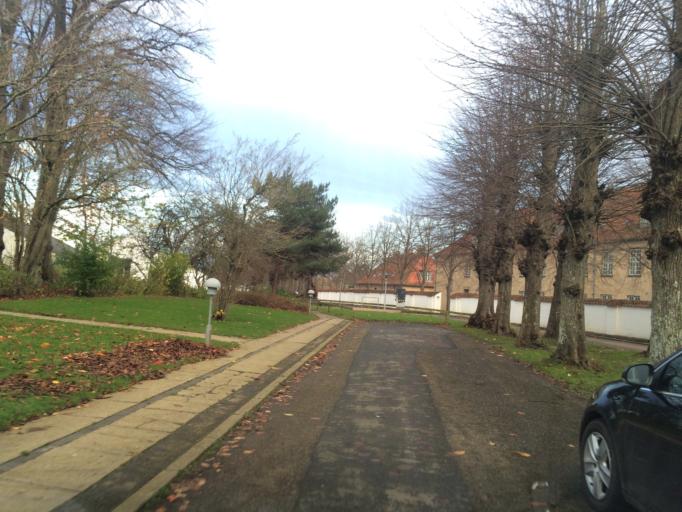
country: DK
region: South Denmark
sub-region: Sonderborg Kommune
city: Augustenborg
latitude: 54.9455
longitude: 9.8619
